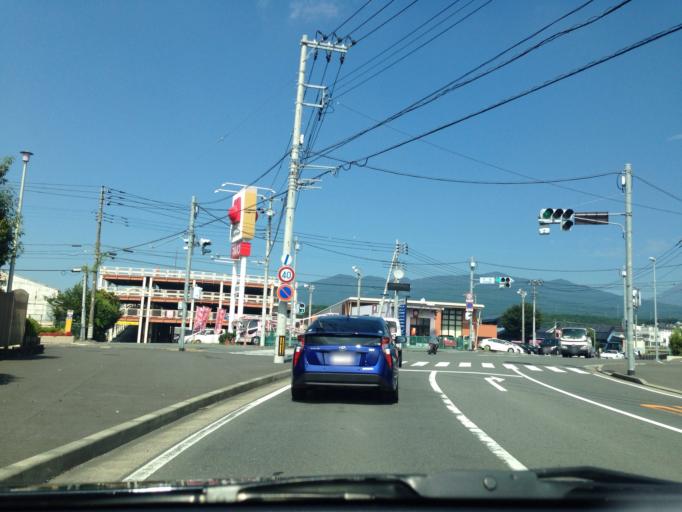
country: JP
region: Shizuoka
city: Mishima
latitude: 35.1645
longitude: 138.9080
